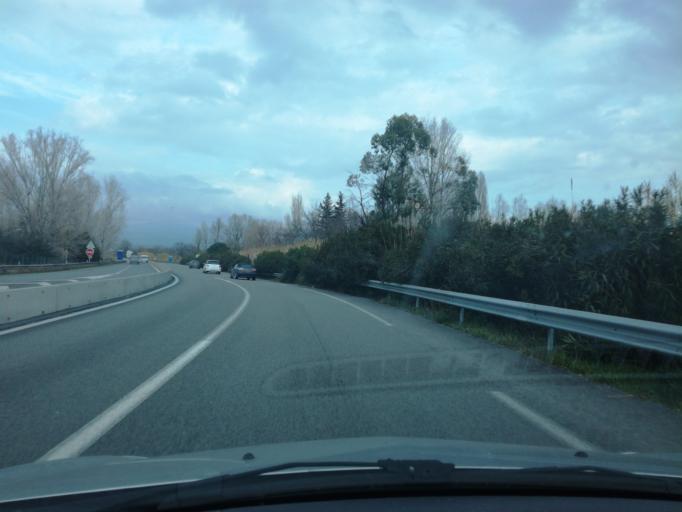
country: FR
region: Provence-Alpes-Cote d'Azur
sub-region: Departement des Alpes-Maritimes
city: Mandelieu-la-Napoule
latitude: 43.5584
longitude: 6.9550
